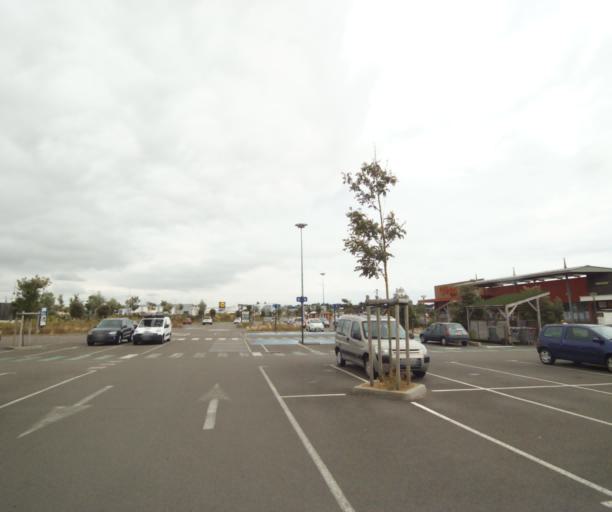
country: FR
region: Pays de la Loire
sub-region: Departement de la Vendee
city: Chateau-d'Olonne
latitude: 46.4877
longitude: -1.7477
